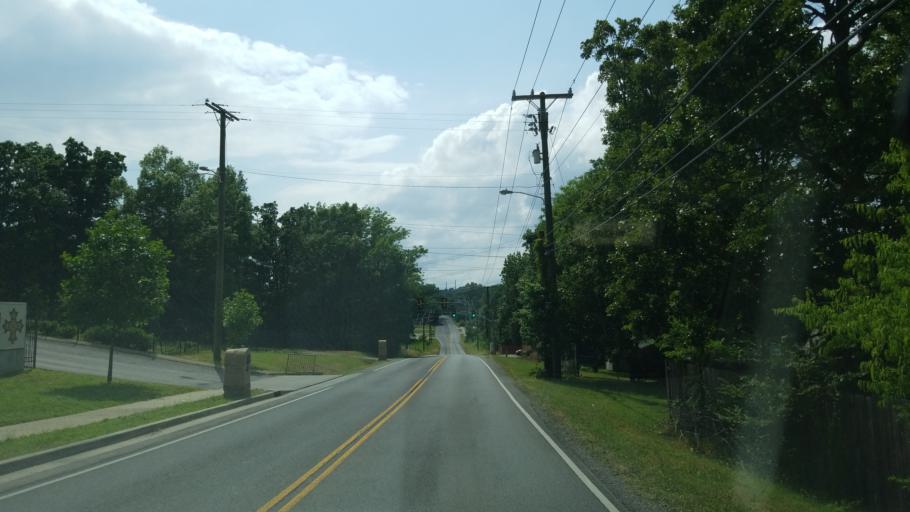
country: US
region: Tennessee
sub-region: Rutherford County
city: La Vergne
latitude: 36.0647
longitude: -86.6210
